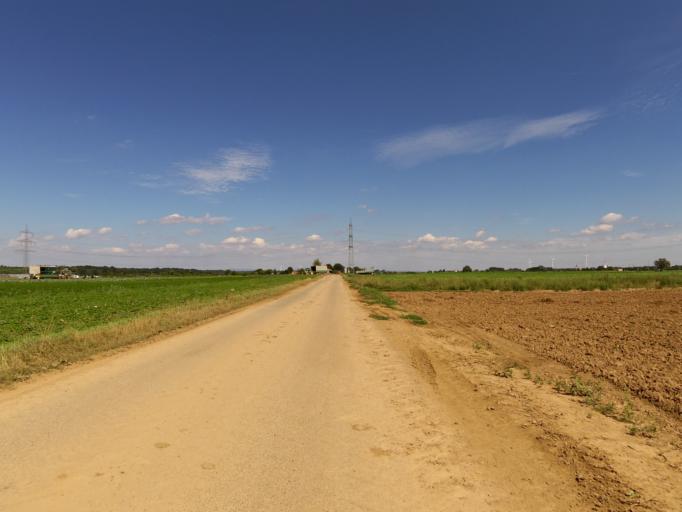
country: DE
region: Rheinland-Pfalz
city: Weingarten
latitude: 49.2694
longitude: 8.2953
